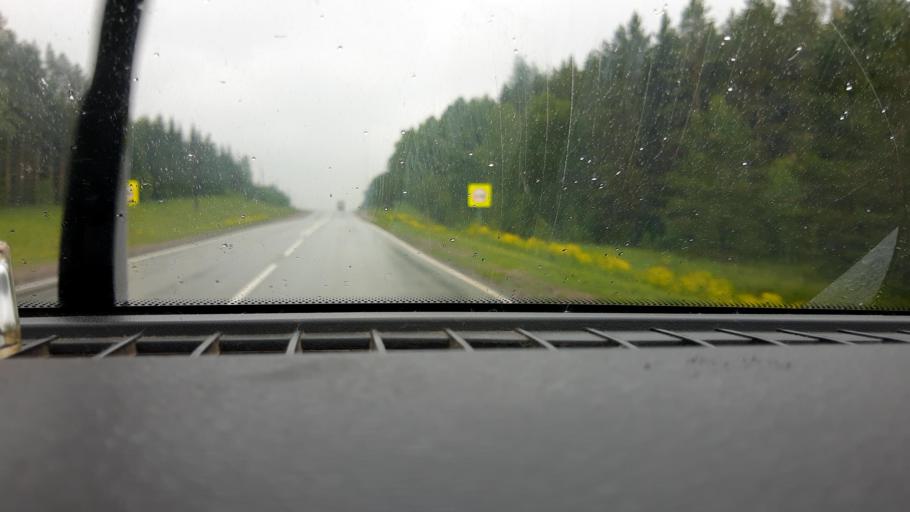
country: RU
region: Bashkortostan
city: Belebey
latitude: 54.2147
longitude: 54.0763
